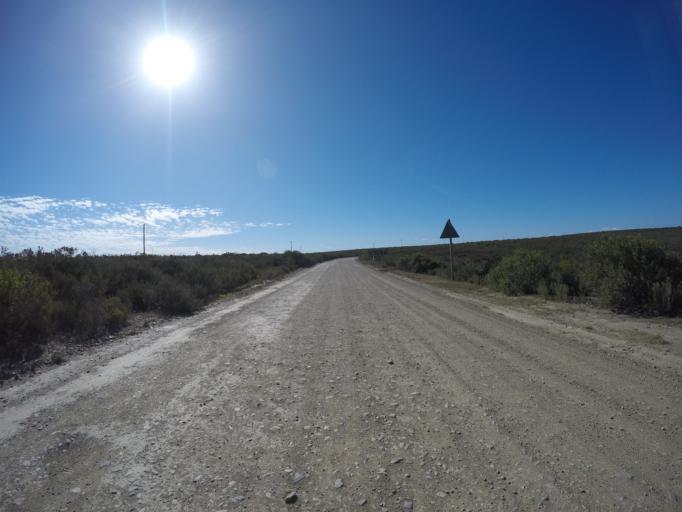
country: ZA
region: Western Cape
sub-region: Overberg District Municipality
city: Bredasdorp
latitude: -34.4213
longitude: 20.4084
